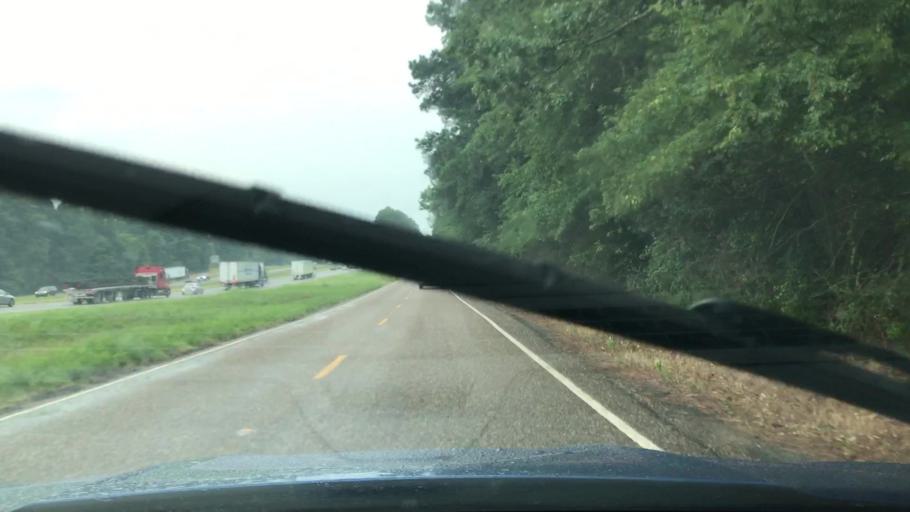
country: US
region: Texas
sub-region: Harrison County
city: Waskom
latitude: 32.4853
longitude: -94.1232
